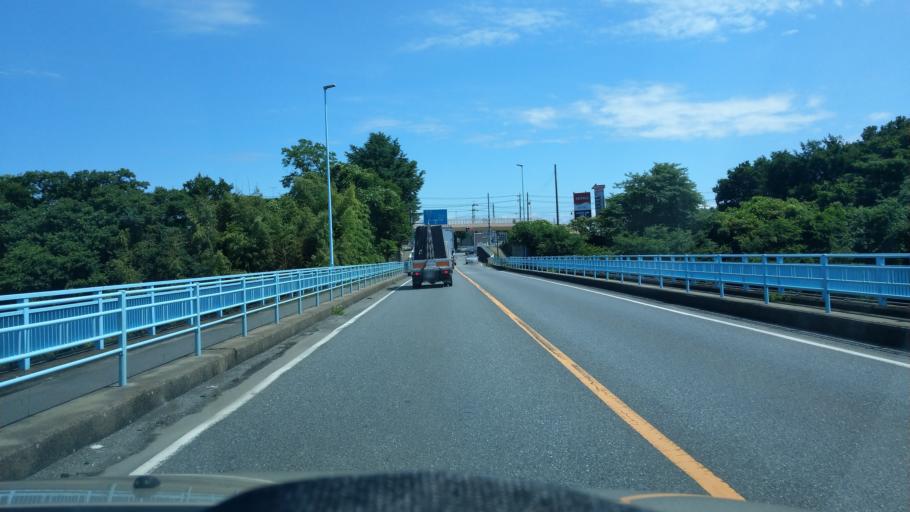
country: JP
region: Saitama
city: Yorii
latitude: 36.1207
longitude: 139.2117
